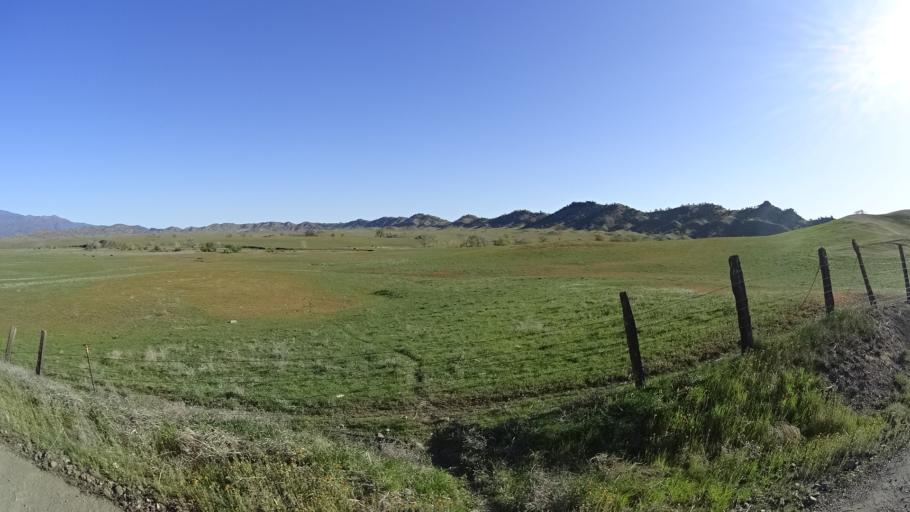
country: US
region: California
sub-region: Tehama County
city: Rancho Tehama Reserve
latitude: 39.7948
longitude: -122.5438
